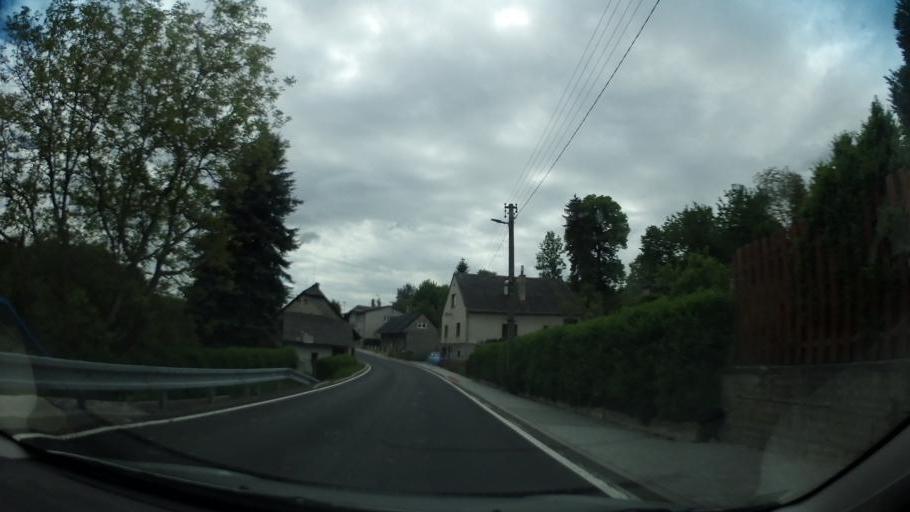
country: CZ
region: Pardubicky
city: Kuncina
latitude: 49.8515
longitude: 16.6957
